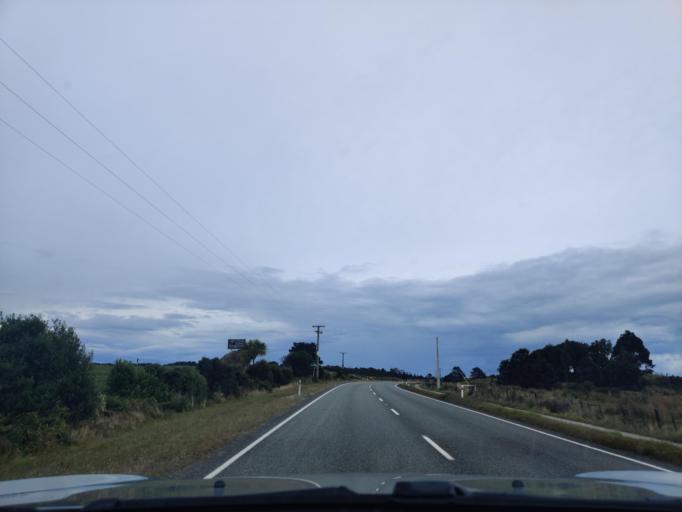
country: NZ
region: West Coast
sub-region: Westland District
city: Hokitika
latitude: -42.8158
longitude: 170.8965
